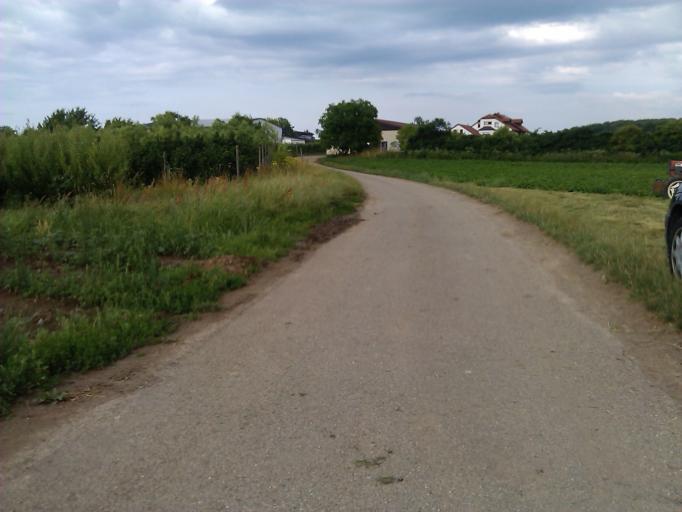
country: DE
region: Baden-Wuerttemberg
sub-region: Regierungsbezirk Stuttgart
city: Lauffen am Neckar
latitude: 49.0649
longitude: 9.1535
